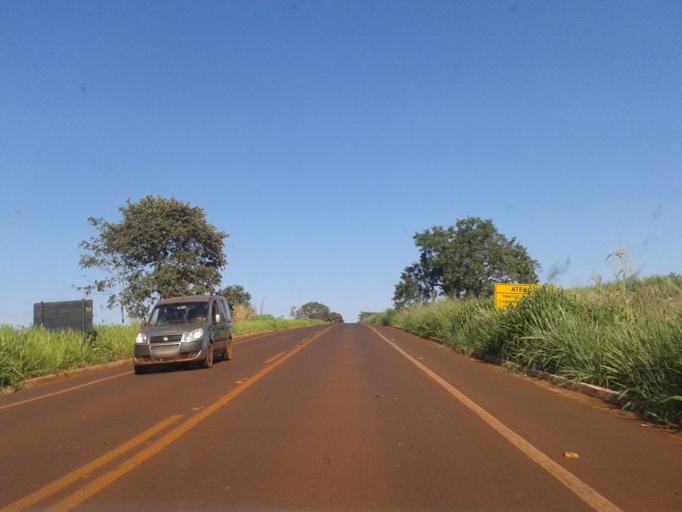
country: BR
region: Minas Gerais
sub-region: Capinopolis
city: Capinopolis
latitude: -18.7030
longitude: -49.6714
